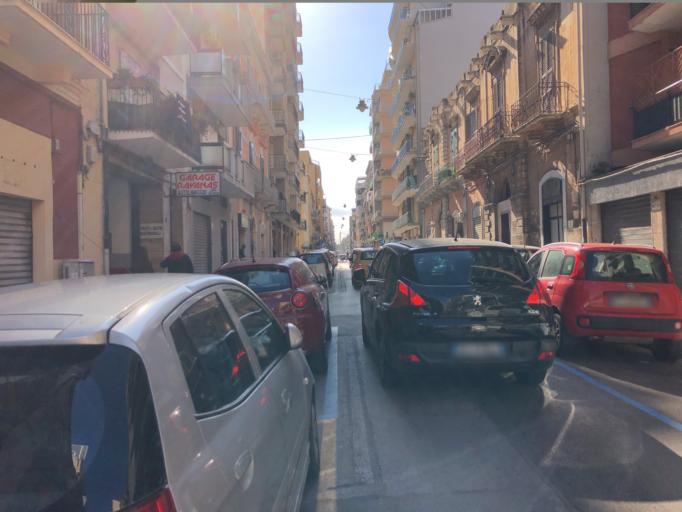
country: IT
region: Apulia
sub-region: Provincia di Bari
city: Bari
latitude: 41.1261
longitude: 16.8584
